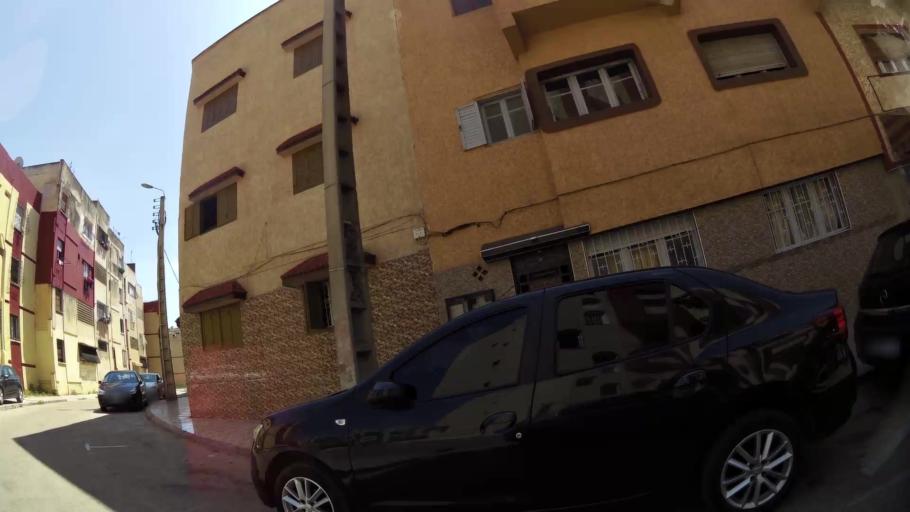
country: MA
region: Rabat-Sale-Zemmour-Zaer
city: Sale
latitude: 34.0454
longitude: -6.7901
